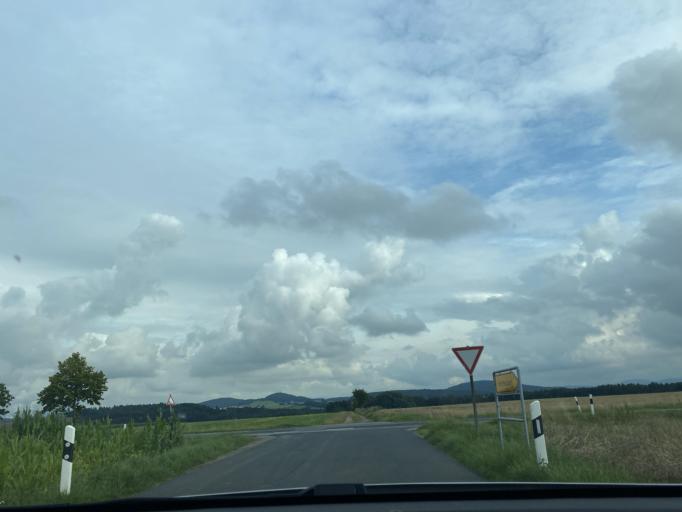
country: DE
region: Saxony
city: Herrnhut
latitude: 51.0188
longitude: 14.7624
